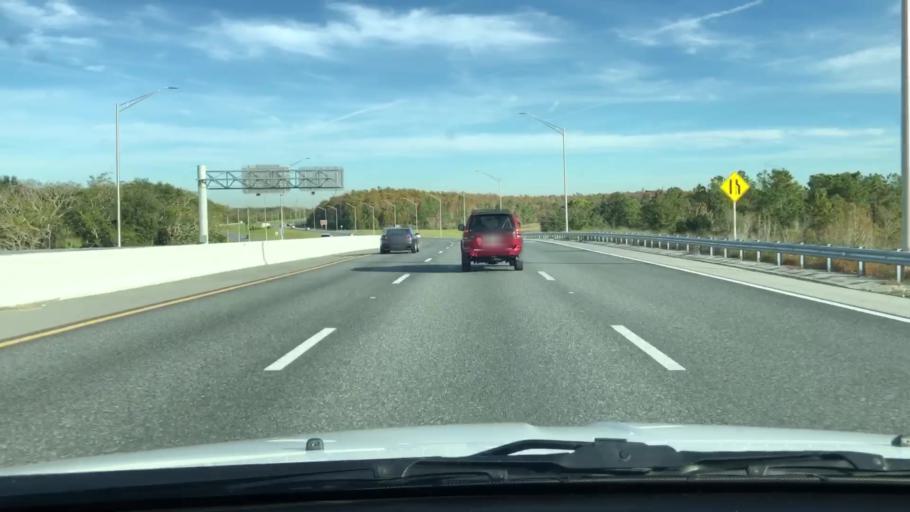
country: US
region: Florida
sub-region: Orange County
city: Meadow Woods
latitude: 28.3844
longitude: -81.3085
